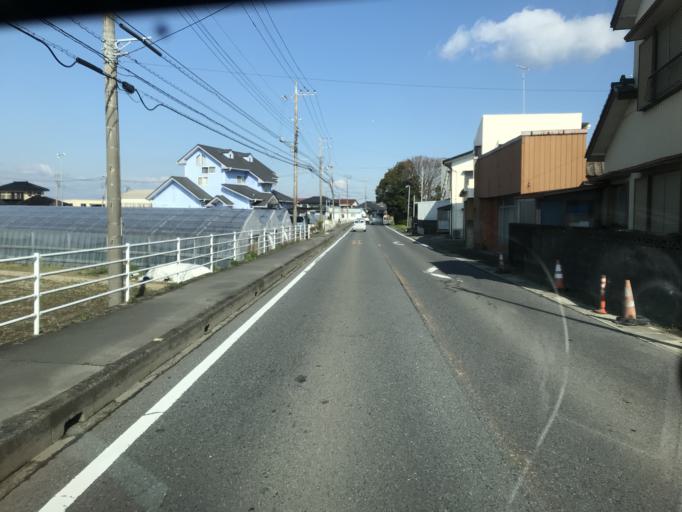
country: JP
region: Ibaraki
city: Itako
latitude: 35.9929
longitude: 140.4749
